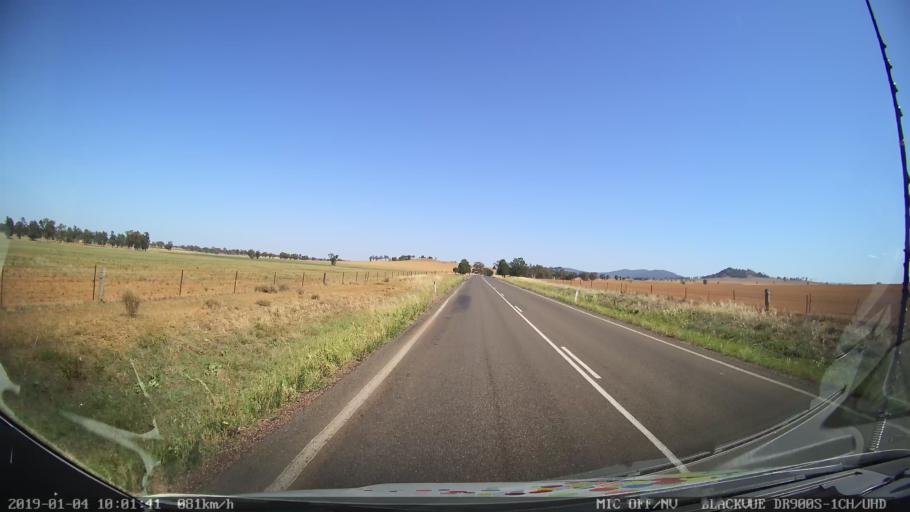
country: AU
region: New South Wales
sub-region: Cabonne
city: Canowindra
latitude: -33.4850
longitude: 148.3684
